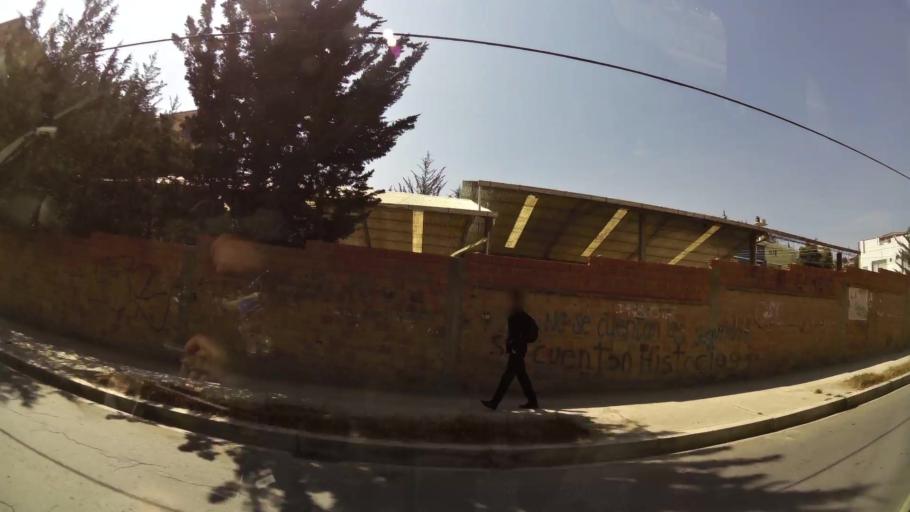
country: BO
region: La Paz
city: La Paz
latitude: -16.5457
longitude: -68.0657
